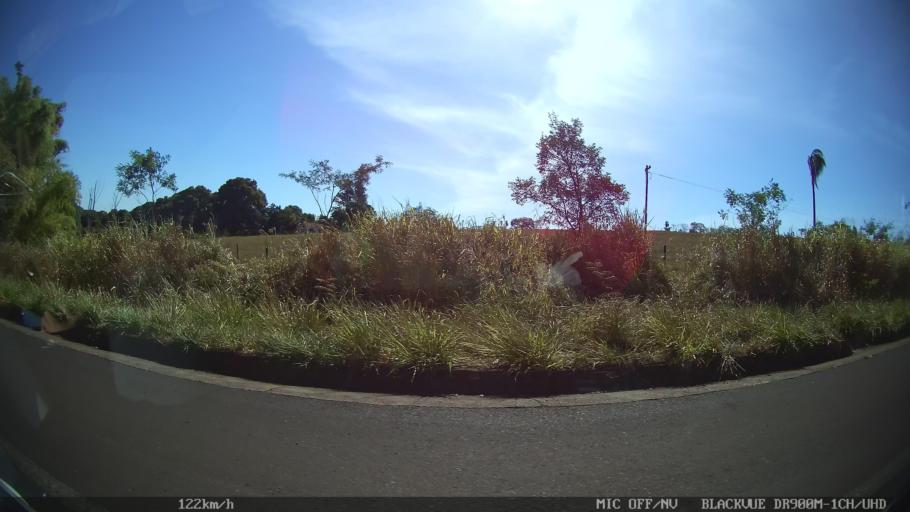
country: BR
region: Sao Paulo
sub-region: Barretos
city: Barretos
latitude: -20.6135
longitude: -48.7564
